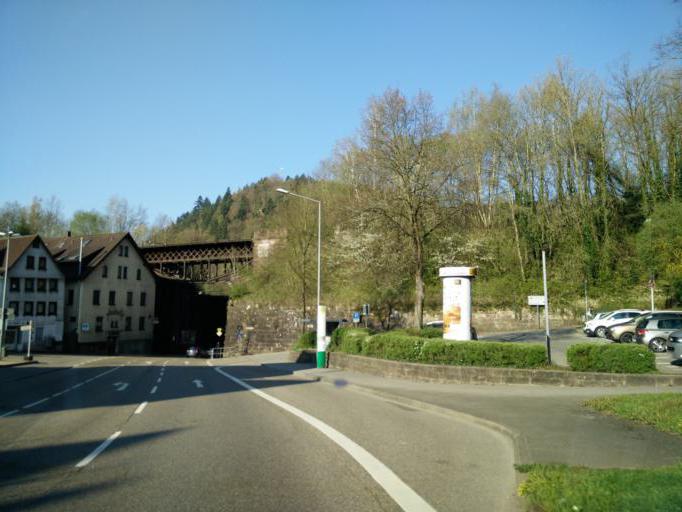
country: DE
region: Baden-Wuerttemberg
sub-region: Karlsruhe Region
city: Calw
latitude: 48.7134
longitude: 8.7441
